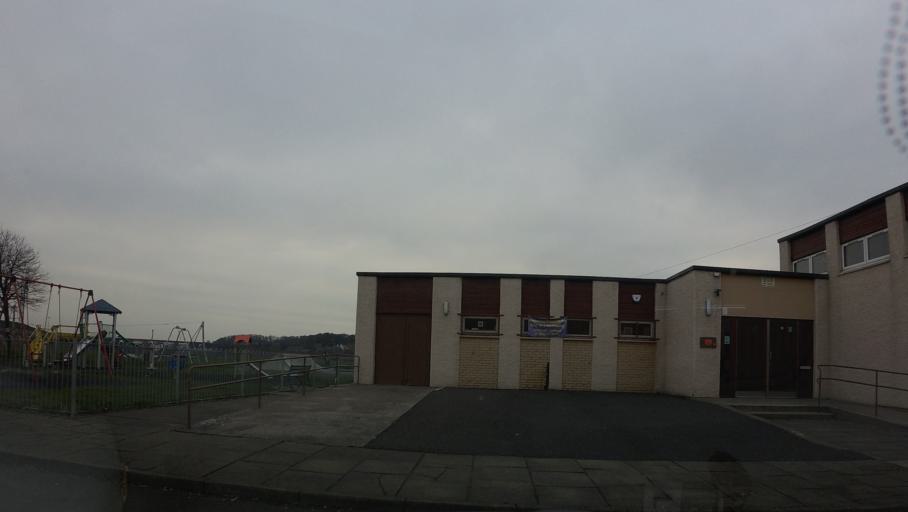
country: GB
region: Scotland
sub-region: Fife
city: Inverkeithing
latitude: 56.0272
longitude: -3.3902
